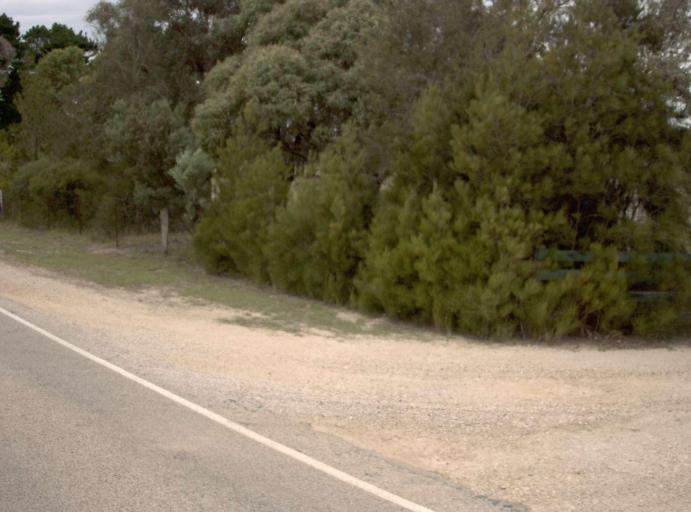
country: AU
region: Victoria
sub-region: East Gippsland
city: Bairnsdale
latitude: -37.8681
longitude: 147.5617
